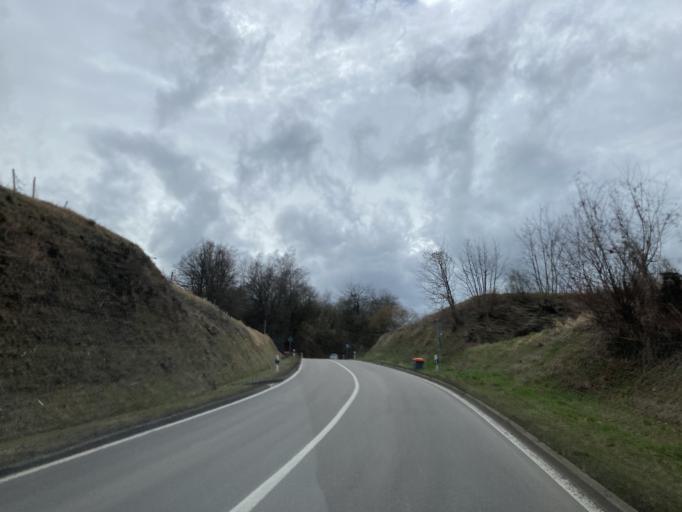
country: DE
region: Baden-Wuerttemberg
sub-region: Freiburg Region
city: Botzingen
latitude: 48.0866
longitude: 7.6935
